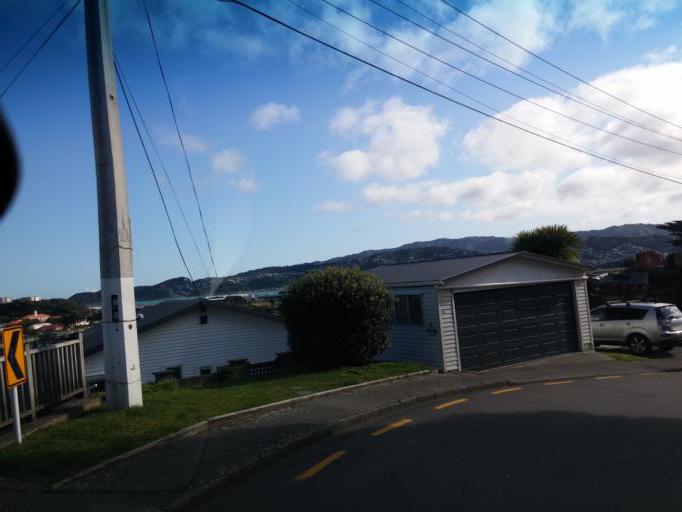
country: NZ
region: Wellington
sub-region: Wellington City
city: Wellington
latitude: -41.3238
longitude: 174.8253
